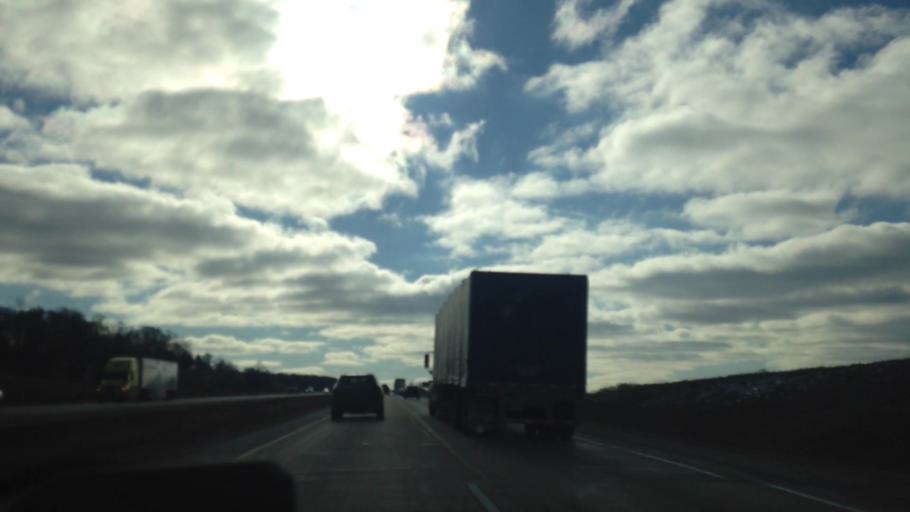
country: US
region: Wisconsin
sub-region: Washington County
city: Slinger
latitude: 43.3773
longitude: -88.3033
